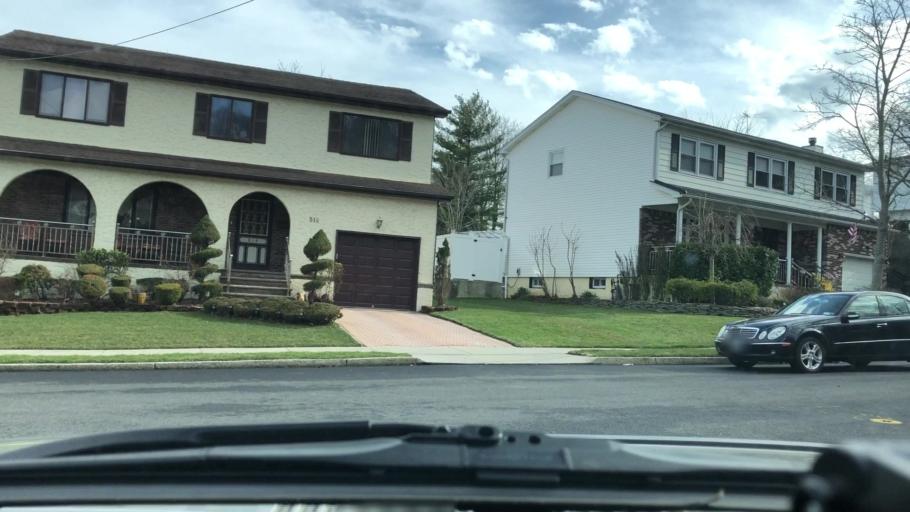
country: US
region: New York
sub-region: Richmond County
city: Staten Island
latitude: 40.6024
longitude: -74.1000
